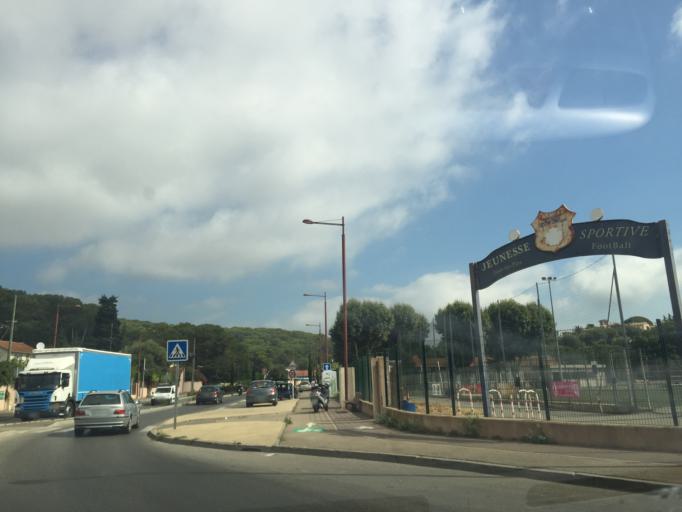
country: FR
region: Provence-Alpes-Cote d'Azur
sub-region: Departement des Alpes-Maritimes
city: Vallauris
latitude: 43.5811
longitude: 7.0899
